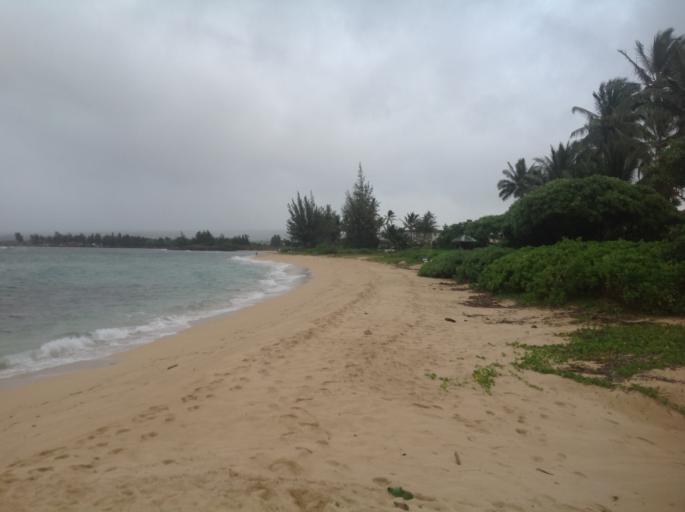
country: US
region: Hawaii
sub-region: Honolulu County
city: Waialua
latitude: 21.5823
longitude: -158.1300
